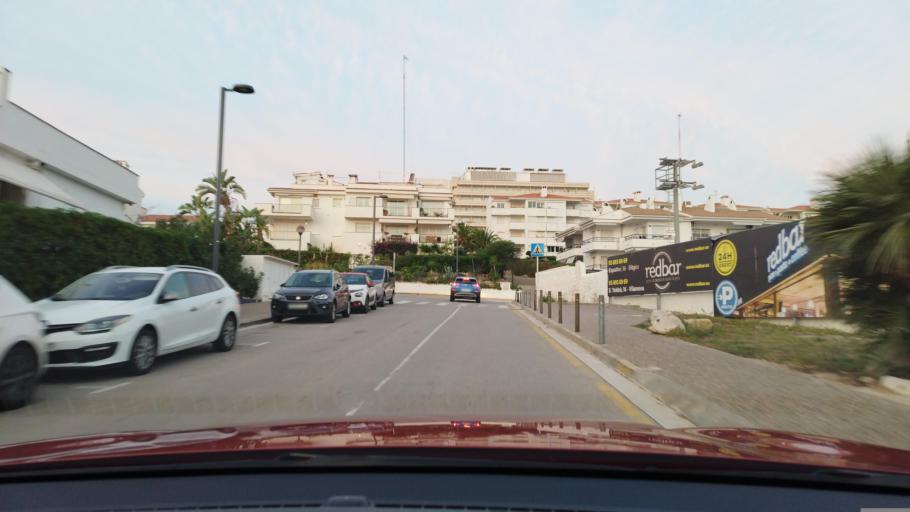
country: ES
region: Catalonia
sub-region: Provincia de Barcelona
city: Sitges
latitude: 41.2363
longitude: 1.8263
